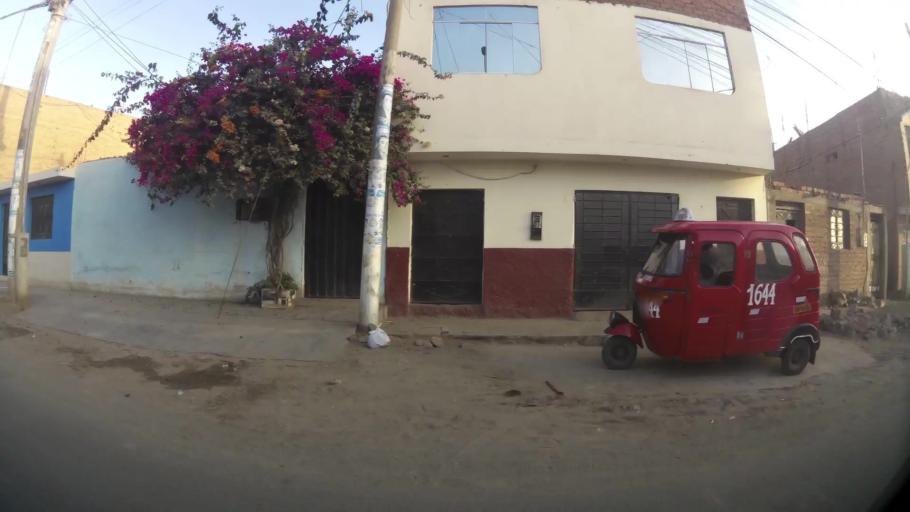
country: PE
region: Lima
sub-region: Huaura
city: Hualmay
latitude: -11.1027
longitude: -77.6121
